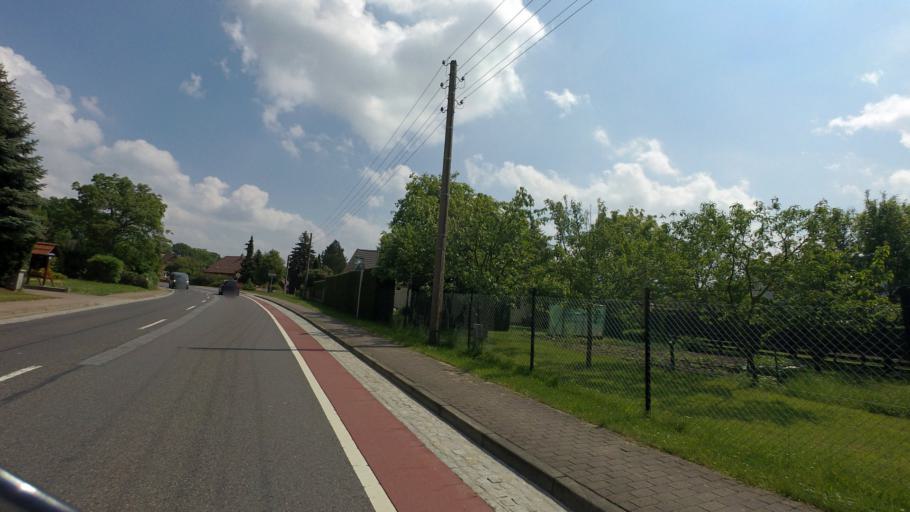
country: DE
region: Saxony
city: Schleife
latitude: 51.5458
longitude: 14.5350
